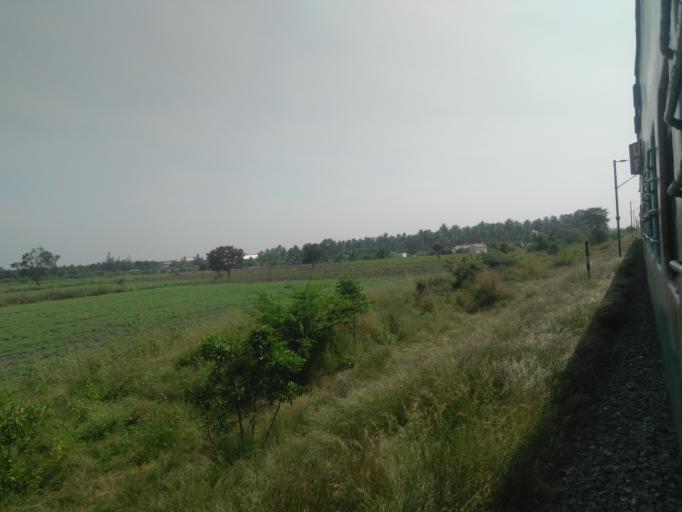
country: IN
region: Tamil Nadu
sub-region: Coimbatore
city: Periyanayakkanpalaiyam
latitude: 11.1370
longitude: 76.9487
